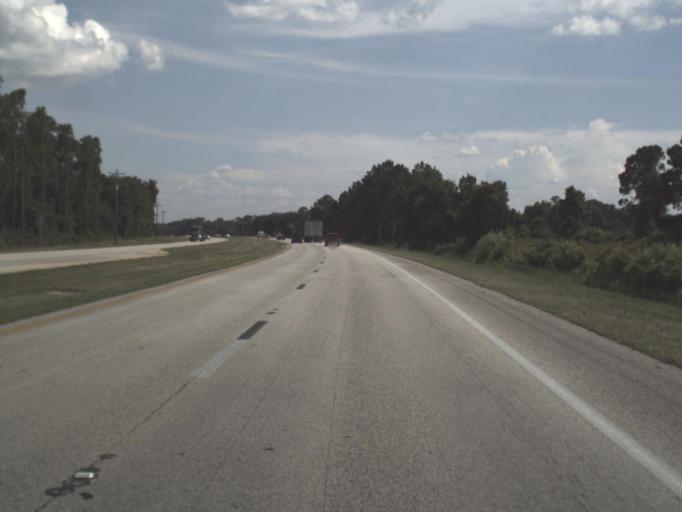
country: US
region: Florida
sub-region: Alachua County
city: Hawthorne
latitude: 29.5258
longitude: -82.1027
